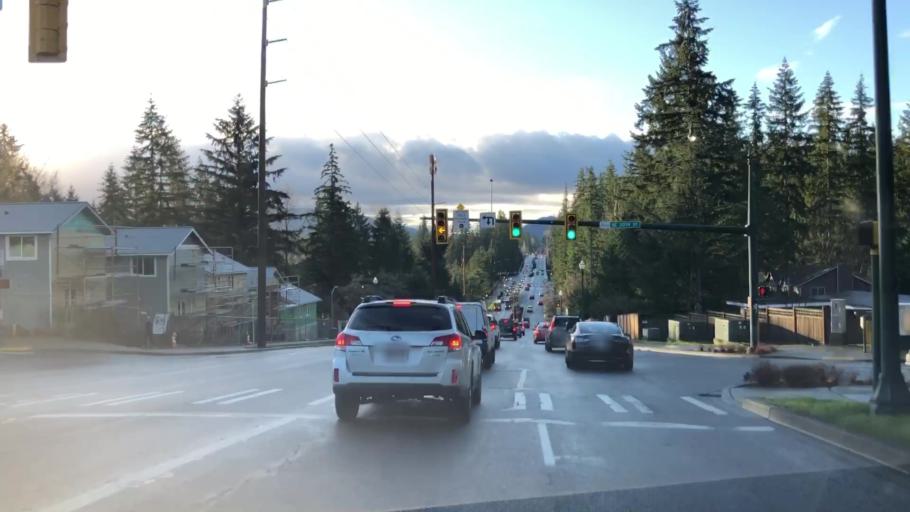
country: US
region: Washington
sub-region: King County
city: City of Sammamish
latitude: 47.5920
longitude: -122.0355
